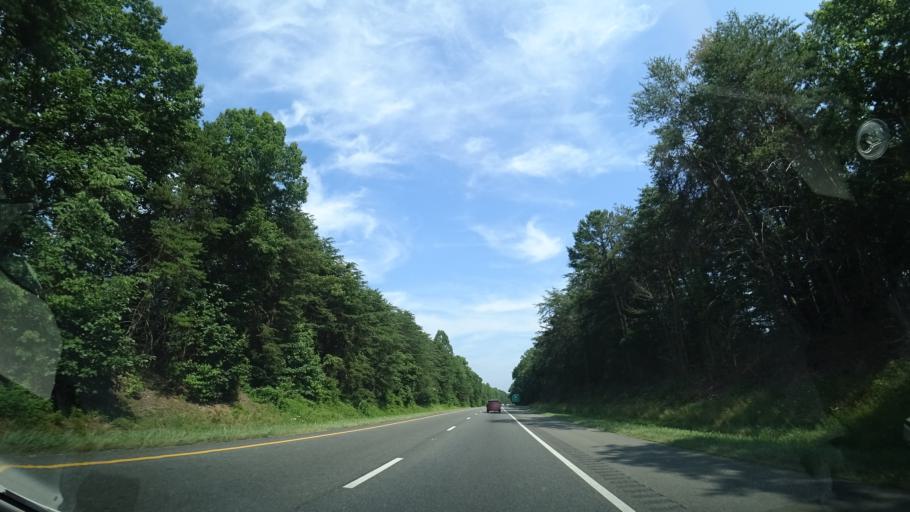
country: US
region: Virginia
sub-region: Goochland County
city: Goochland
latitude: 37.7948
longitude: -77.9066
